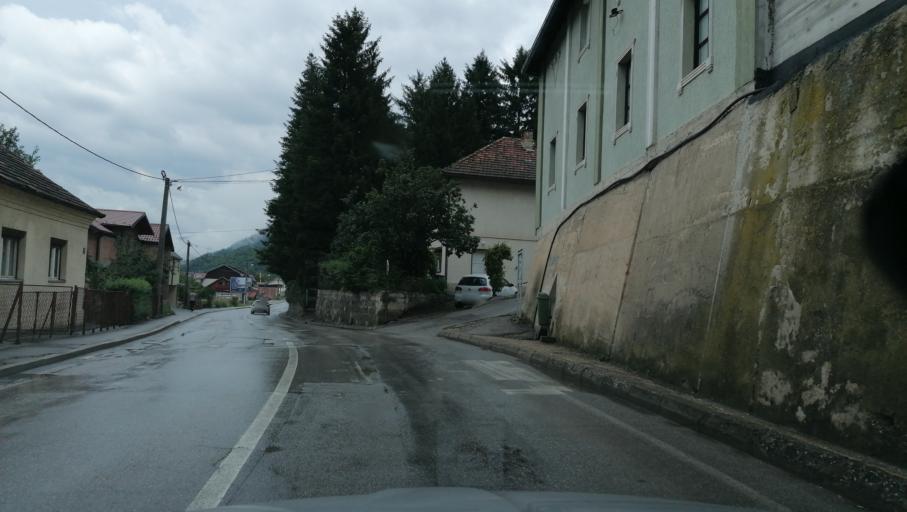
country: BA
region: Republika Srpska
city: Visegrad
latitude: 43.7870
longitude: 19.2963
